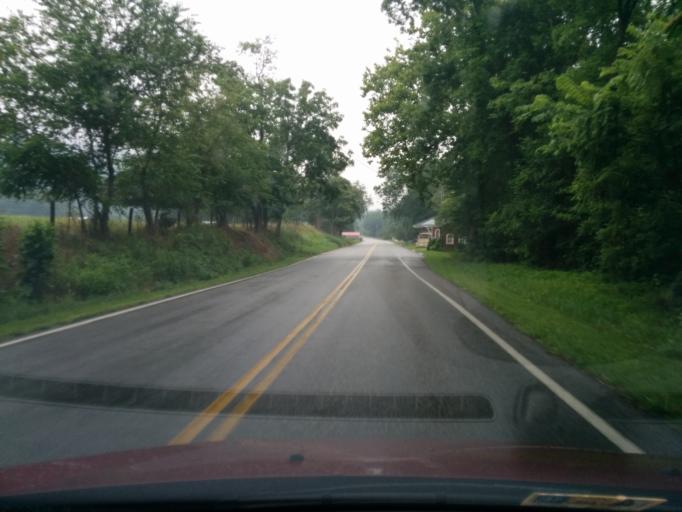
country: US
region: Virginia
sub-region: Rockbridge County
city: East Lexington
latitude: 37.9010
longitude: -79.4102
